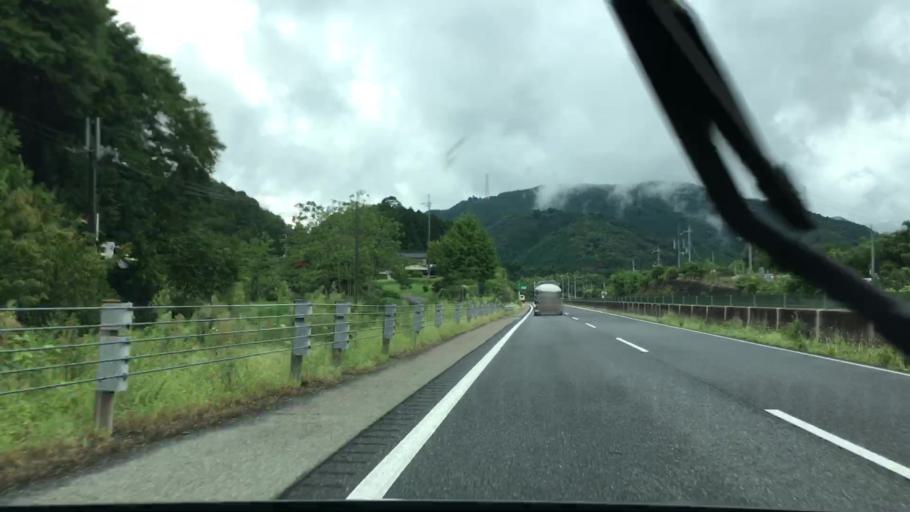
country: JP
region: Hyogo
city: Yamazakicho-nakabirose
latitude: 35.0266
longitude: 134.4908
